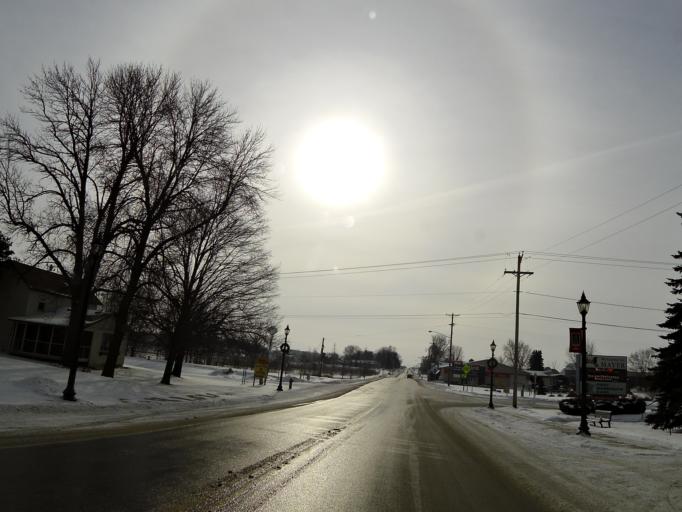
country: US
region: Minnesota
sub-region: Carver County
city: Mayer
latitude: 44.8855
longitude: -93.8881
